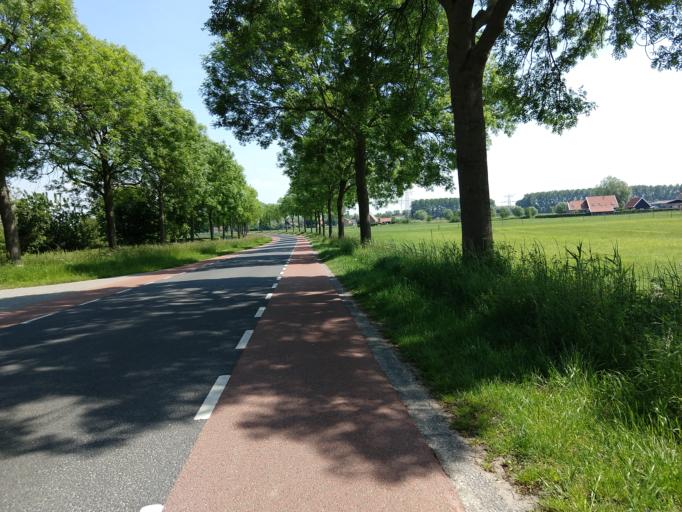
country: NL
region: Zeeland
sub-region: Gemeente Borsele
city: Borssele
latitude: 51.4353
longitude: 3.8072
